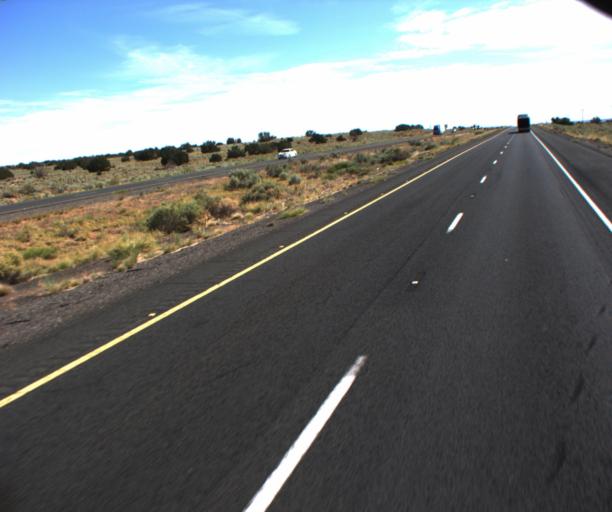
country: US
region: Arizona
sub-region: Apache County
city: Houck
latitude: 35.1538
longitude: -109.5023
